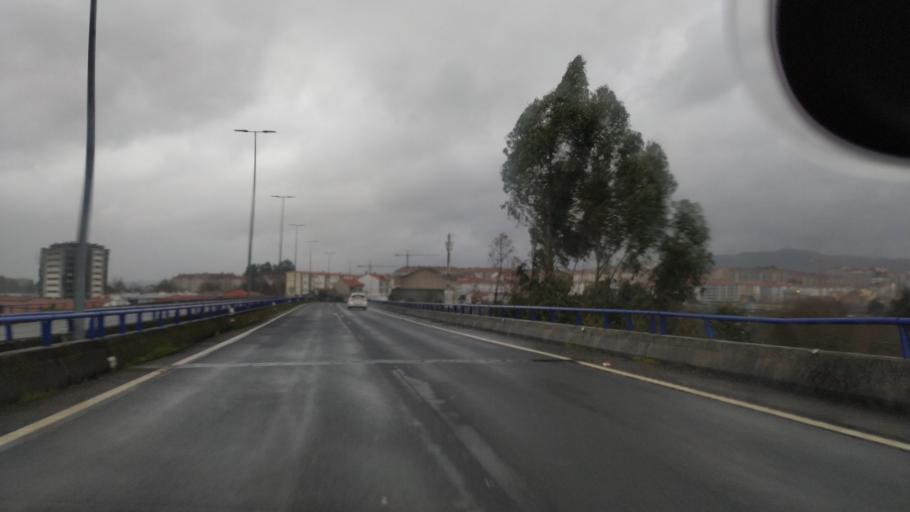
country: ES
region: Galicia
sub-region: Provincia da Coruna
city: Santiago de Compostela
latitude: 42.8624
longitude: -8.5490
